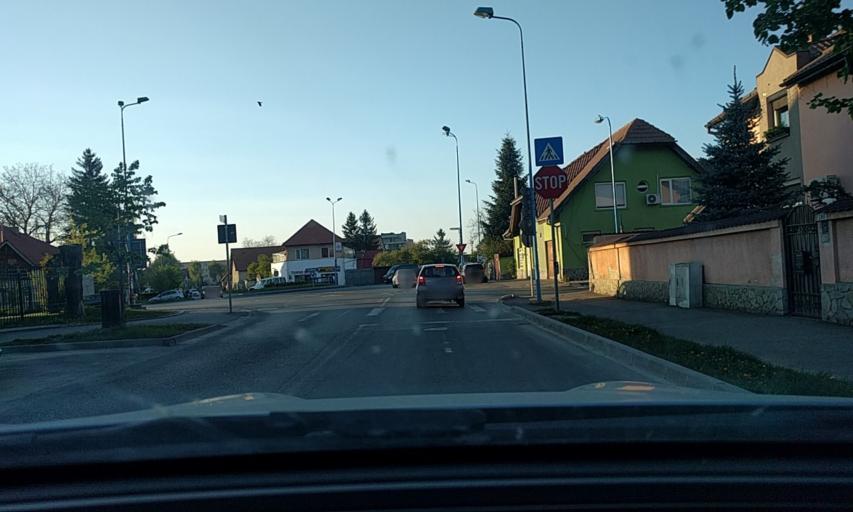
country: RO
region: Brasov
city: Brasov
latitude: 45.6661
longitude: 25.5778
